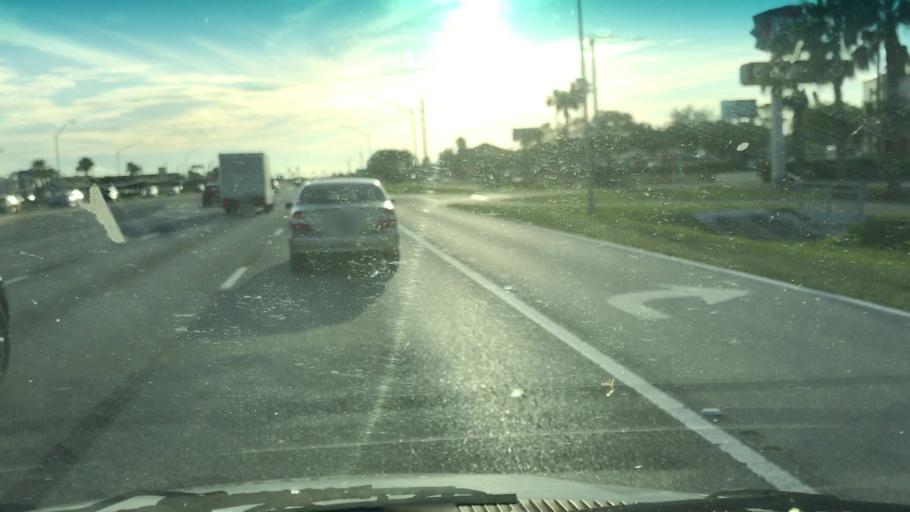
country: US
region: Florida
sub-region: Lee County
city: Fort Myers
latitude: 26.5980
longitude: -81.8470
